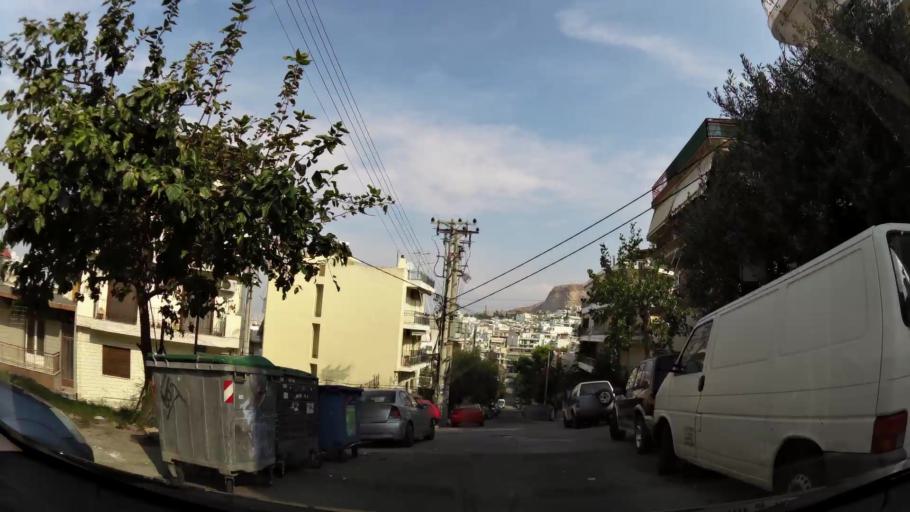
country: GR
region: Attica
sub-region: Nomarchia Athinas
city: Galatsi
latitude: 38.0095
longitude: 23.7553
